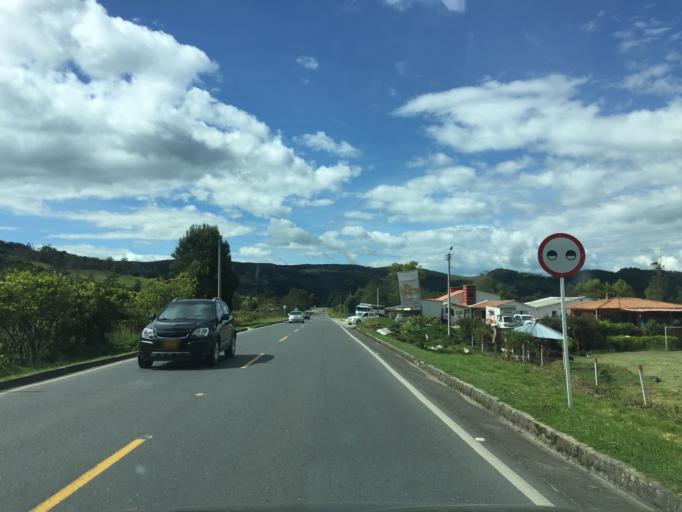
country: CO
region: Boyaca
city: Arcabuco
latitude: 5.7806
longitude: -73.4608
